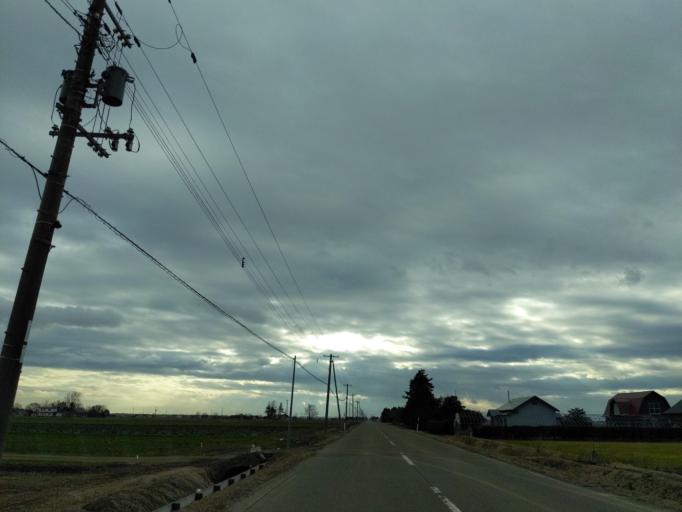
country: JP
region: Hokkaido
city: Kitahiroshima
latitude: 43.0392
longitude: 141.6894
